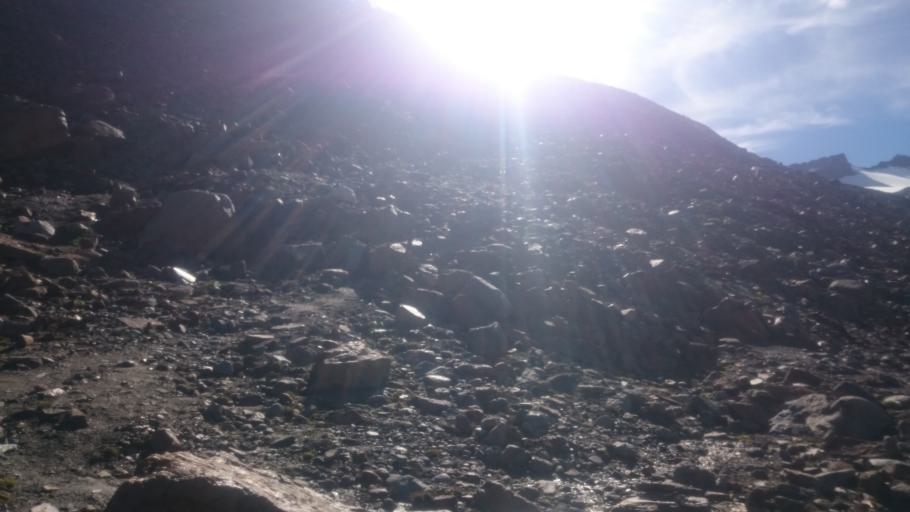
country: IT
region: Trentino-Alto Adige
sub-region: Bolzano
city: Senales
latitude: 46.8650
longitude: 10.8204
